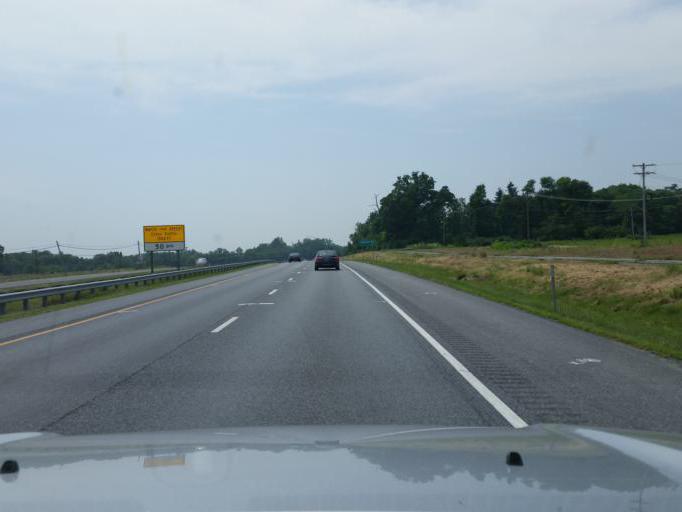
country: US
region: Maryland
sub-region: Frederick County
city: Clover Hill
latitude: 39.4602
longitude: -77.4010
